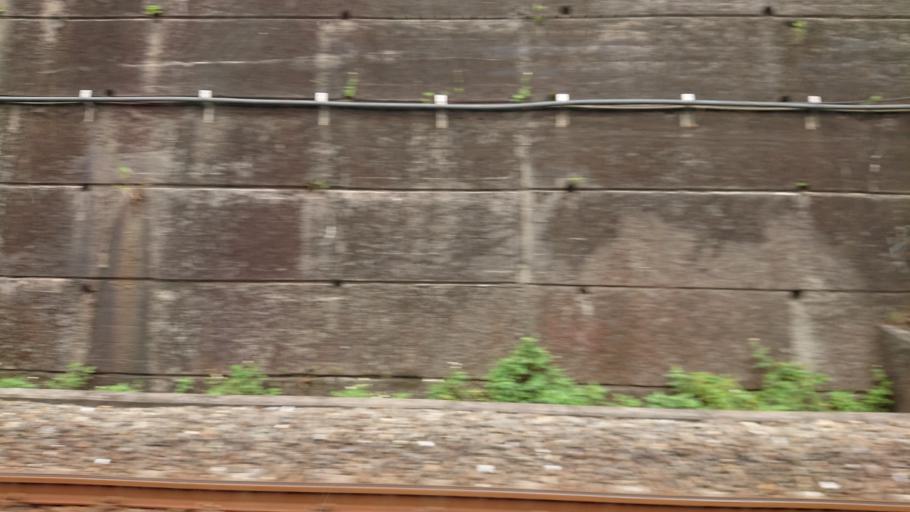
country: TW
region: Taiwan
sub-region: Keelung
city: Keelung
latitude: 25.0045
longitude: 121.9579
